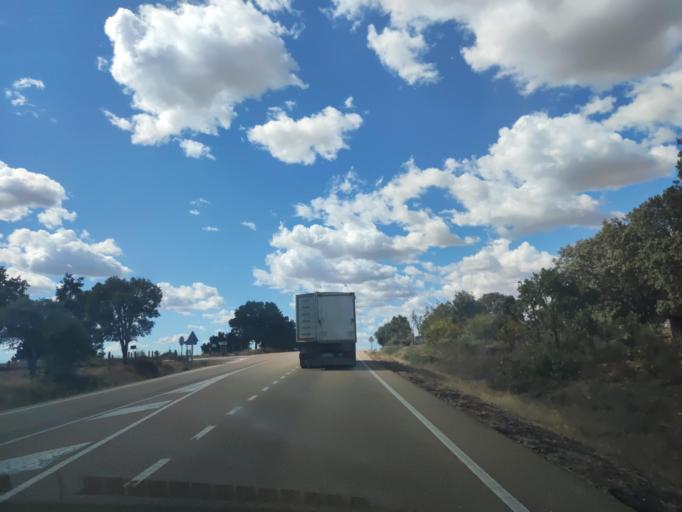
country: ES
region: Castille and Leon
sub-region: Provincia de Salamanca
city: Peralejos de Arriba
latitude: 40.9303
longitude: -6.3393
